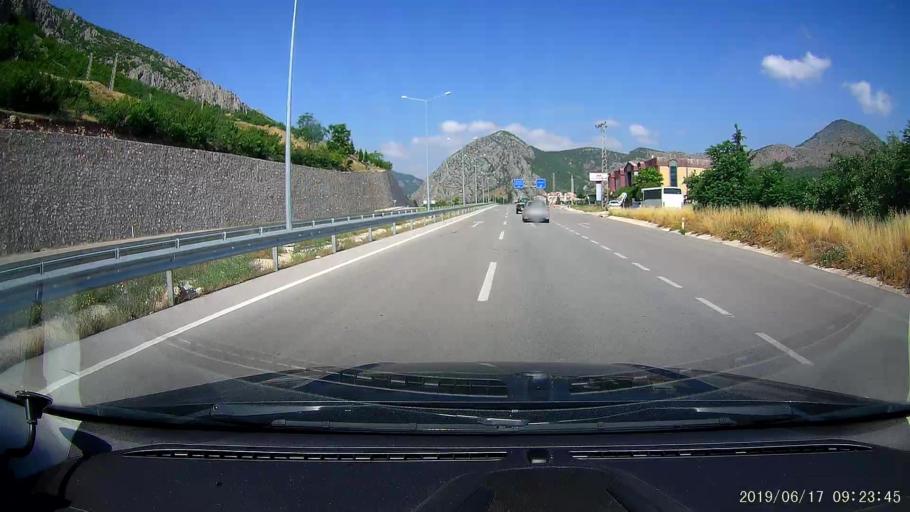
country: TR
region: Amasya
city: Amasya
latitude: 40.6742
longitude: 35.8683
